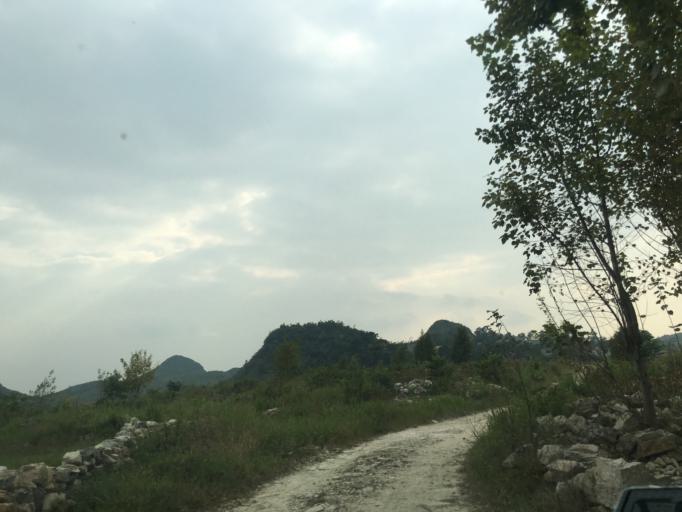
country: CN
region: Guangxi Zhuangzu Zizhiqu
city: Xinzhou
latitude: 25.4457
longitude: 105.6504
